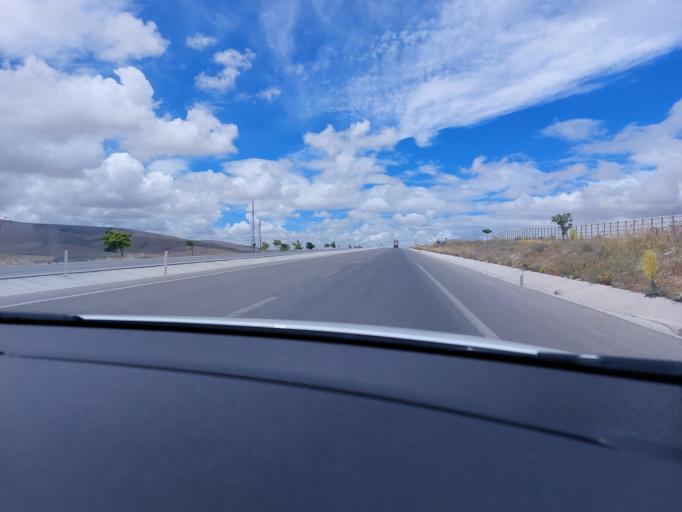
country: TR
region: Konya
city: Obruk
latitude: 38.0608
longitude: 33.0390
